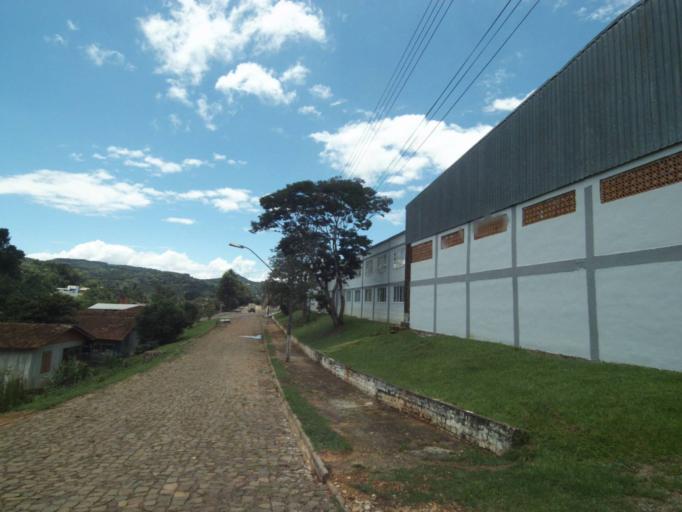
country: BR
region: Parana
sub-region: Uniao Da Vitoria
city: Uniao da Vitoria
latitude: -26.1657
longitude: -51.5531
